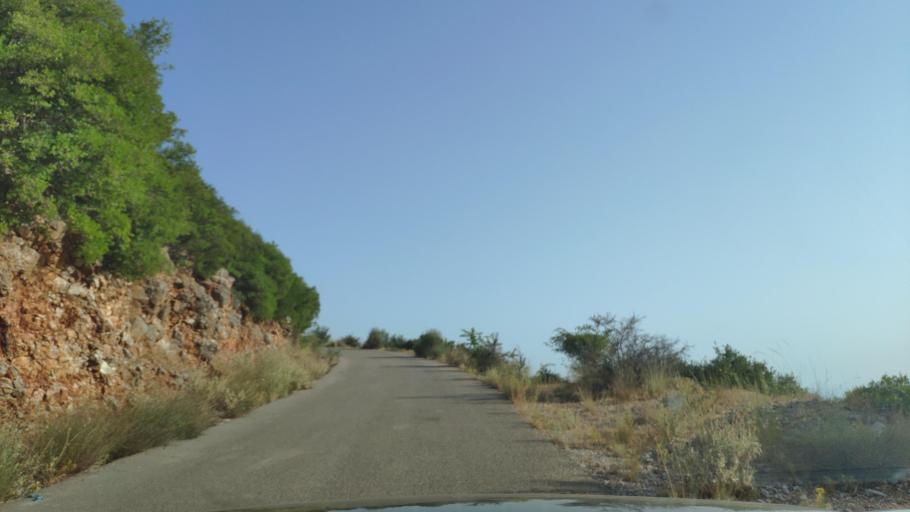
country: GR
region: West Greece
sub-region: Nomos Aitolias kai Akarnanias
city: Monastirakion
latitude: 38.8466
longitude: 20.9769
